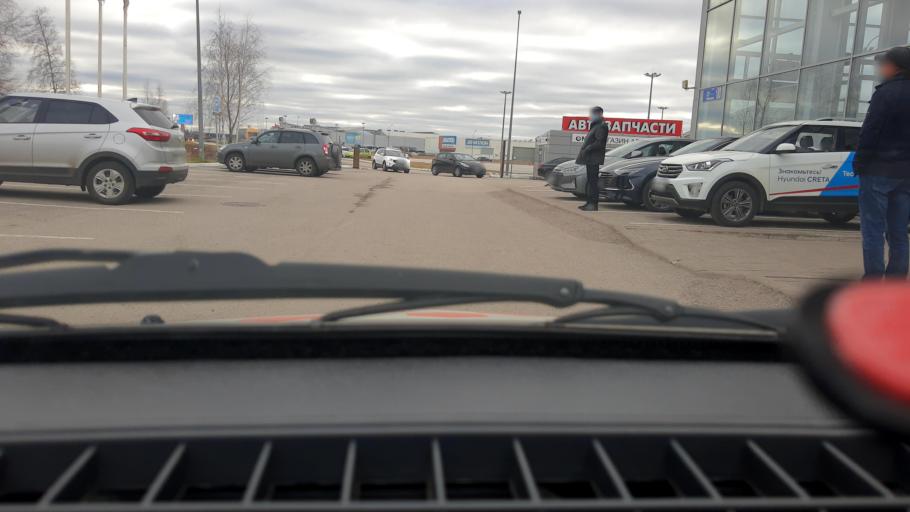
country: RU
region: Bashkortostan
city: Ufa
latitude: 54.6813
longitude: 55.9328
